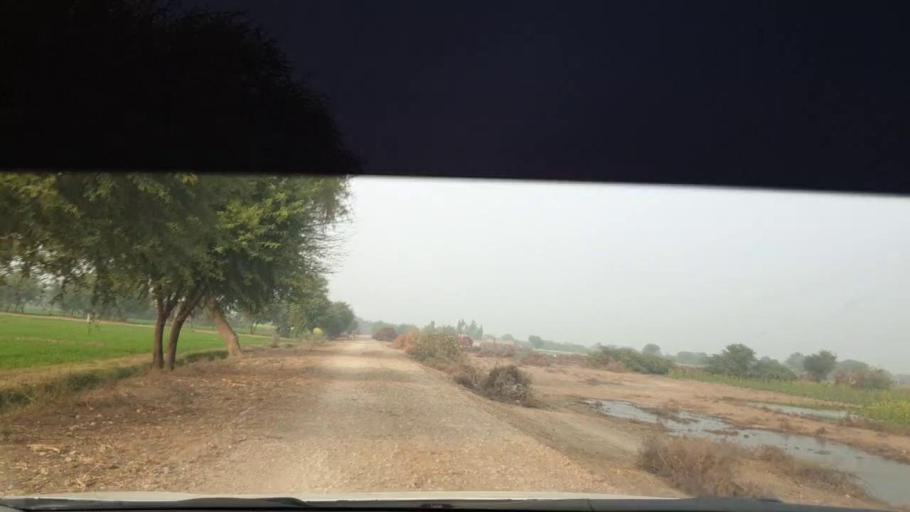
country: PK
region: Sindh
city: Berani
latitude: 25.8270
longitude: 68.8915
